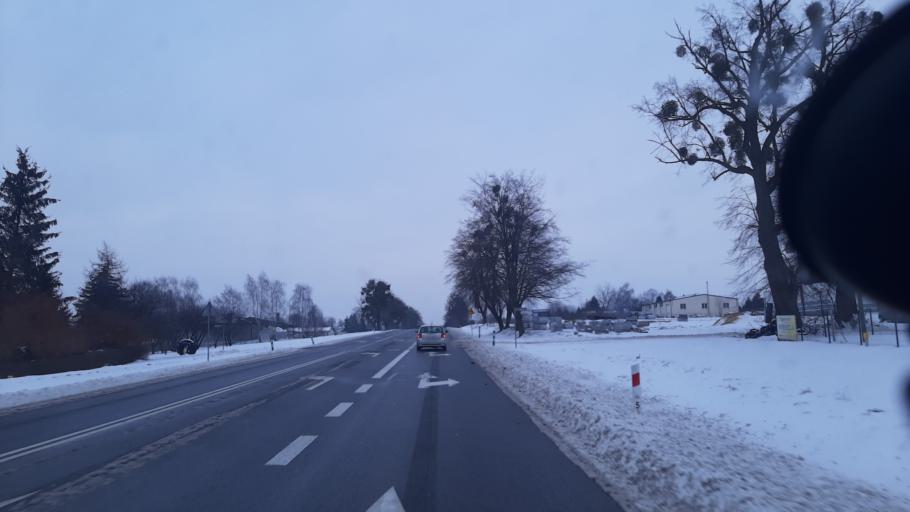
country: PL
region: Lublin Voivodeship
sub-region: Powiat lubelski
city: Garbow
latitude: 51.3597
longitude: 22.3136
